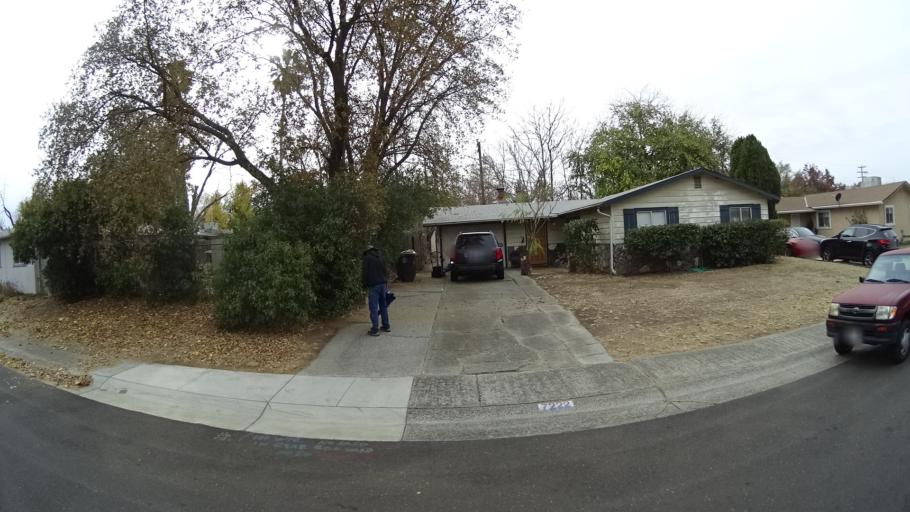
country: US
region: California
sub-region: Sacramento County
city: Citrus Heights
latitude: 38.7094
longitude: -121.3010
